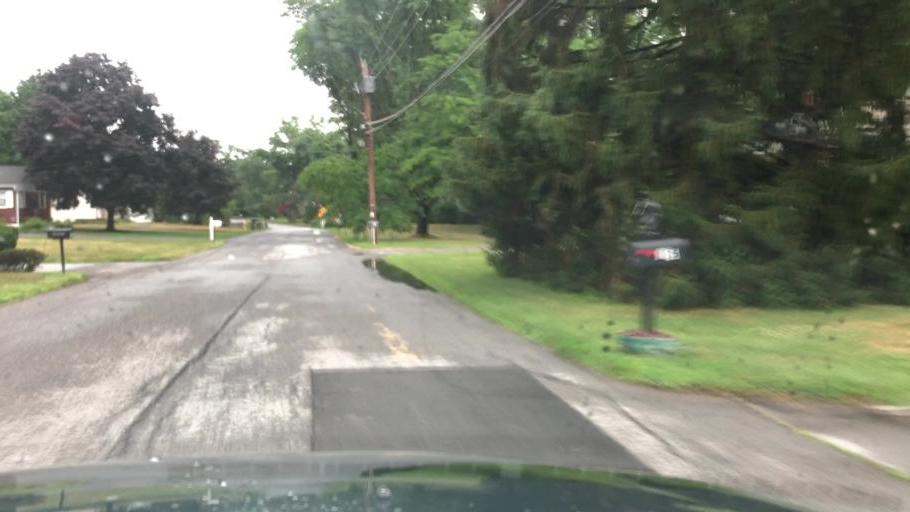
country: US
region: New York
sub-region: Dutchess County
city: Fishkill
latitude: 41.5300
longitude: -73.9110
